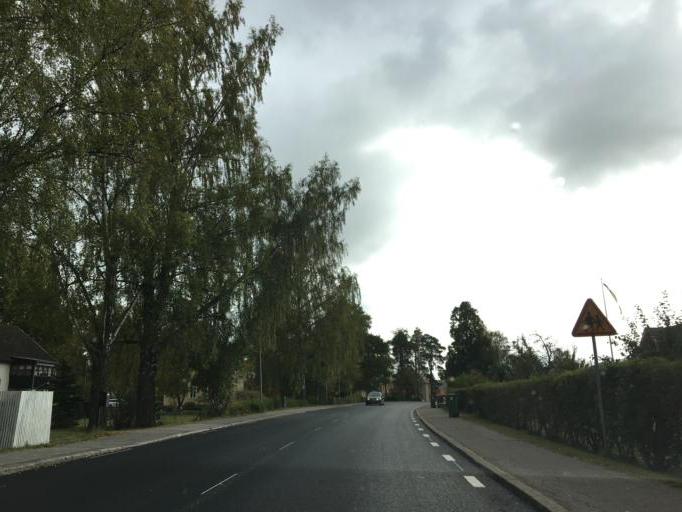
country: SE
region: Soedermanland
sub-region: Nykopings Kommun
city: Stigtomta
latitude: 58.8024
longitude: 16.7860
